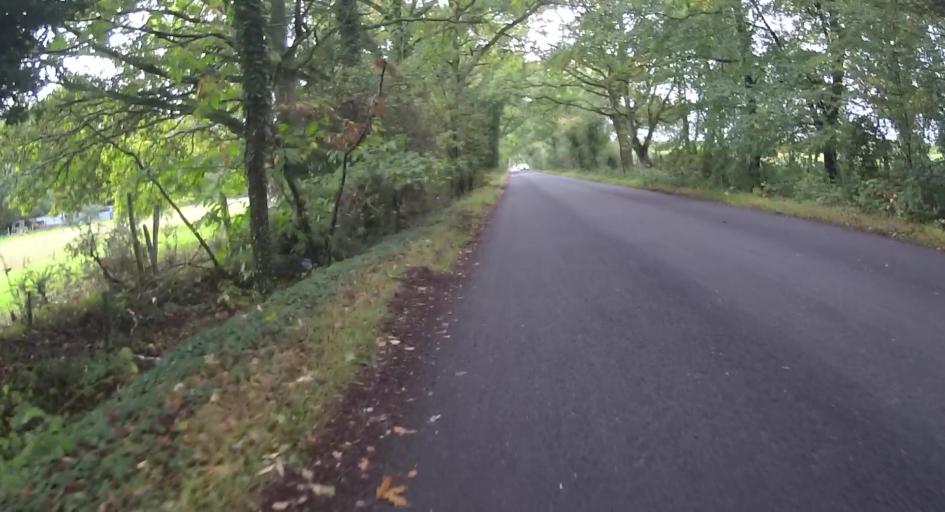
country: GB
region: England
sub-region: Hampshire
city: Tadley
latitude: 51.3584
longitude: -1.1776
